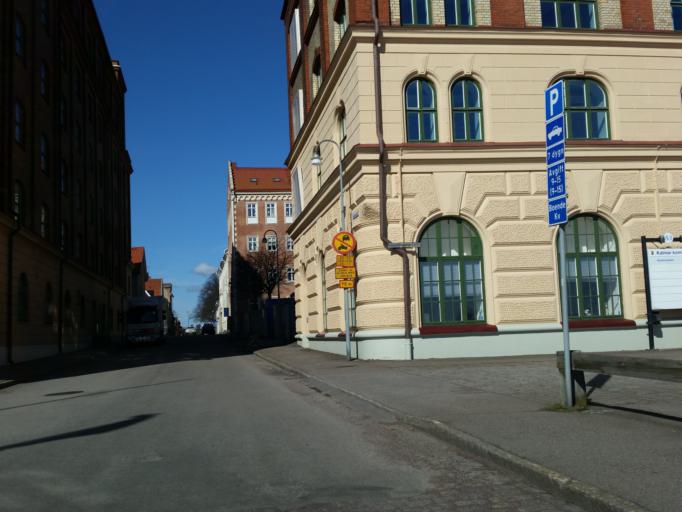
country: SE
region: Kalmar
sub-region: Kalmar Kommun
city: Kalmar
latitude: 56.6641
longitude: 16.3712
